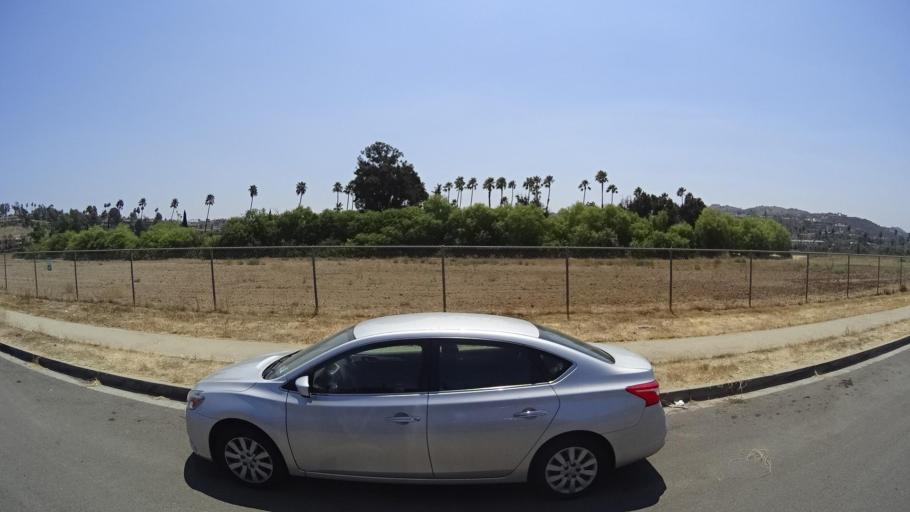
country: US
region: California
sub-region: San Diego County
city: Bonsall
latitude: 33.2930
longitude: -117.2116
